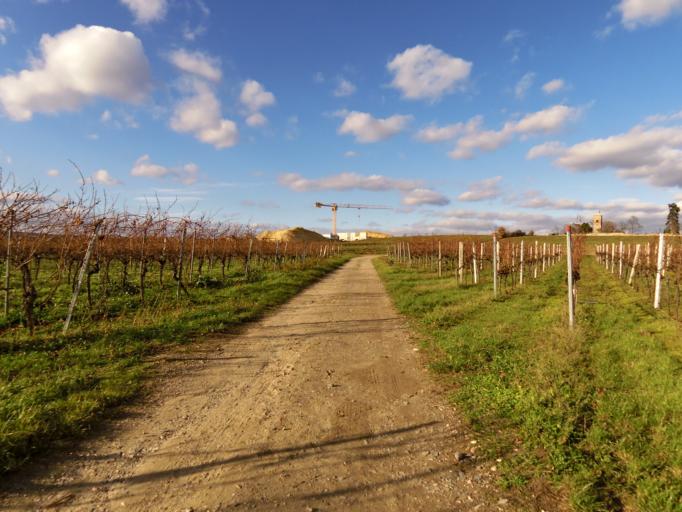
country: DE
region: Rheinland-Pfalz
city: Freinsheim
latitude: 49.4957
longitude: 8.2138
